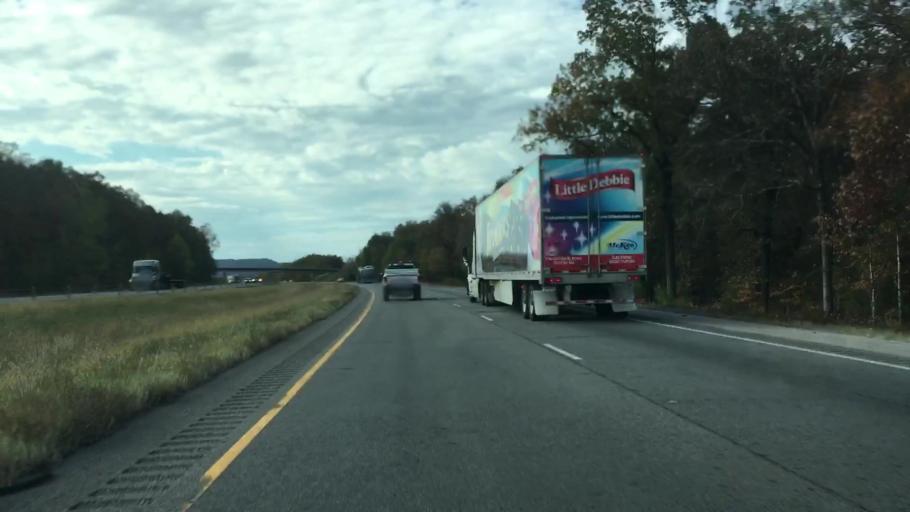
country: US
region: Arkansas
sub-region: Pope County
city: Atkins
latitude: 35.2466
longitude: -92.8677
